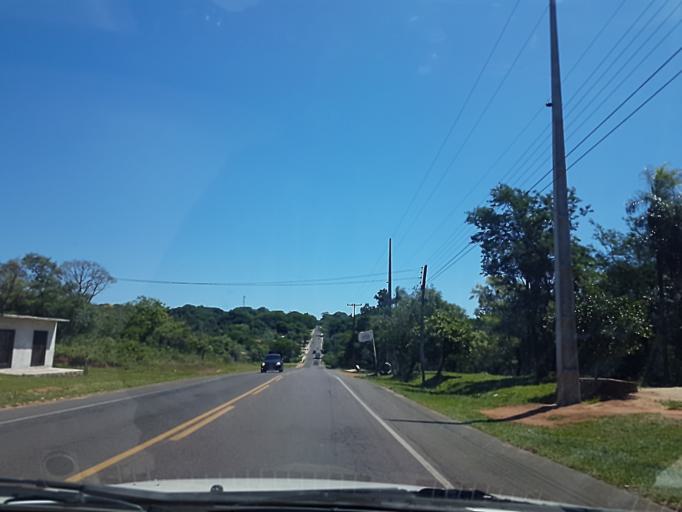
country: PY
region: Cordillera
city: Altos
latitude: -25.2564
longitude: -57.2445
